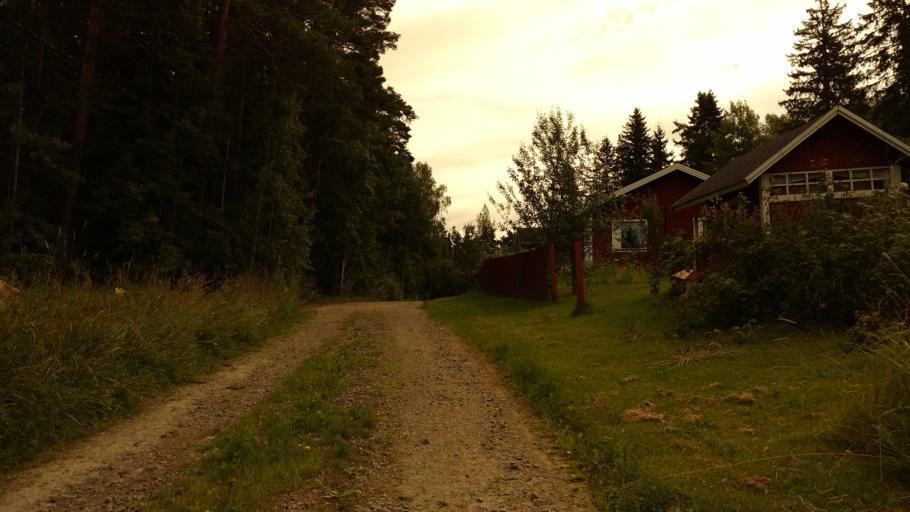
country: FI
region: Varsinais-Suomi
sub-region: Turku
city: Paimio
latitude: 60.4604
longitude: 22.6308
